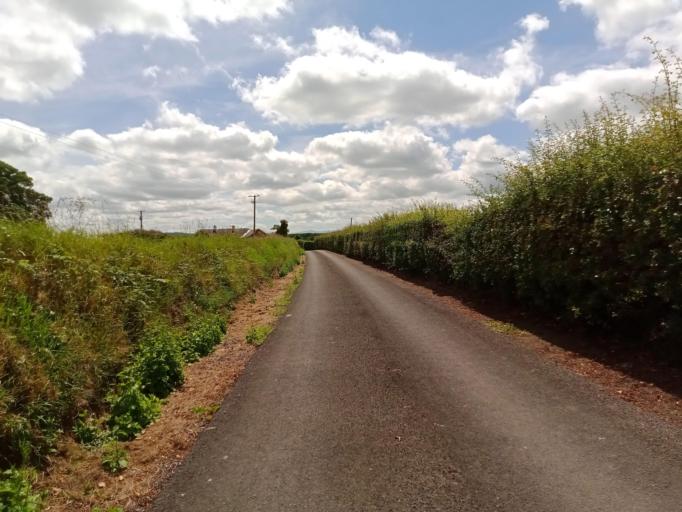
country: IE
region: Leinster
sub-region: Kilkenny
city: Callan
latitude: 52.5465
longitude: -7.4198
